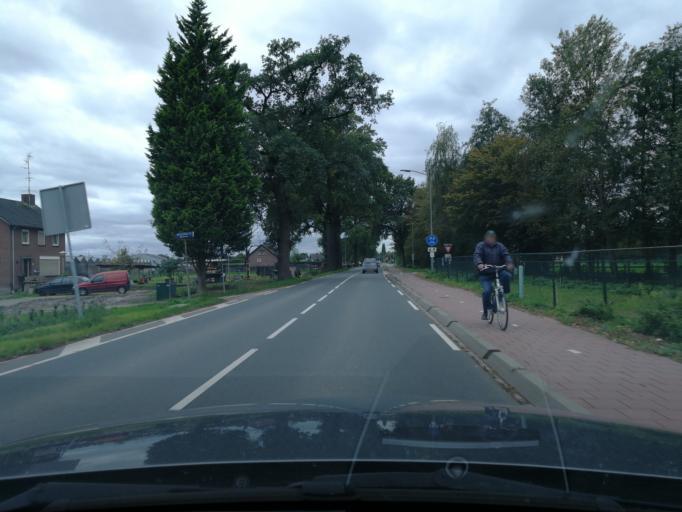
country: NL
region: Limburg
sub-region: Gemeente Venlo
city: Venlo
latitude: 51.3957
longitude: 6.2043
